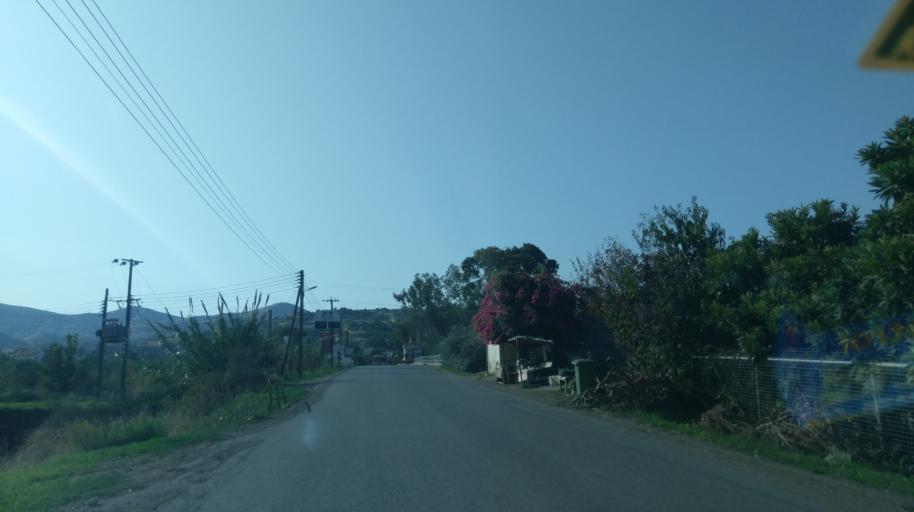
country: CY
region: Lefkosia
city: Kato Pyrgos
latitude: 35.1676
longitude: 32.7408
